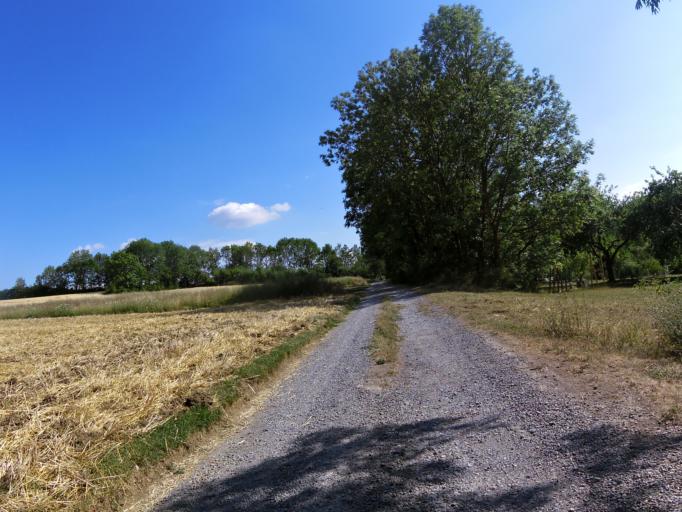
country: DE
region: Bavaria
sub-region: Regierungsbezirk Unterfranken
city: Rimpar
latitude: 49.8340
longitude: 9.9593
